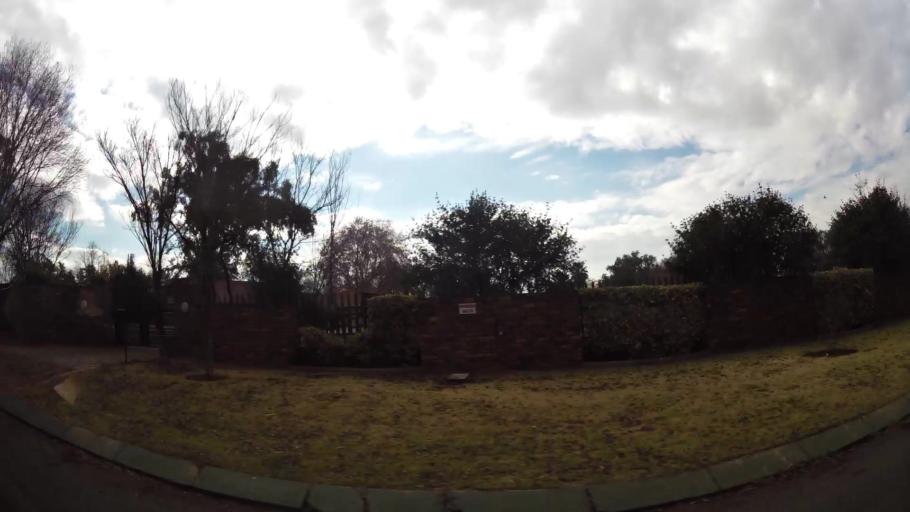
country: ZA
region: Gauteng
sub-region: Sedibeng District Municipality
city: Meyerton
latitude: -26.5884
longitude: 28.0148
